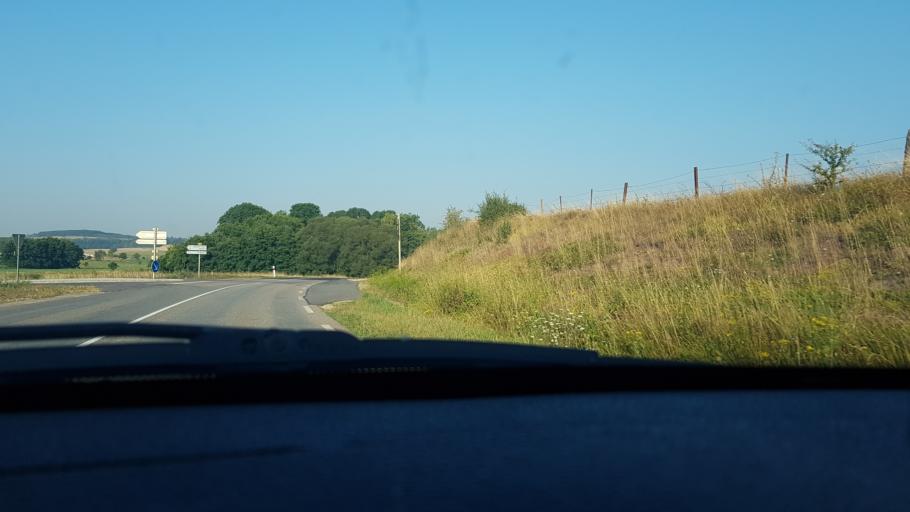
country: FR
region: Lorraine
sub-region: Departement des Vosges
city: Charmes
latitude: 48.3626
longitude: 6.2641
